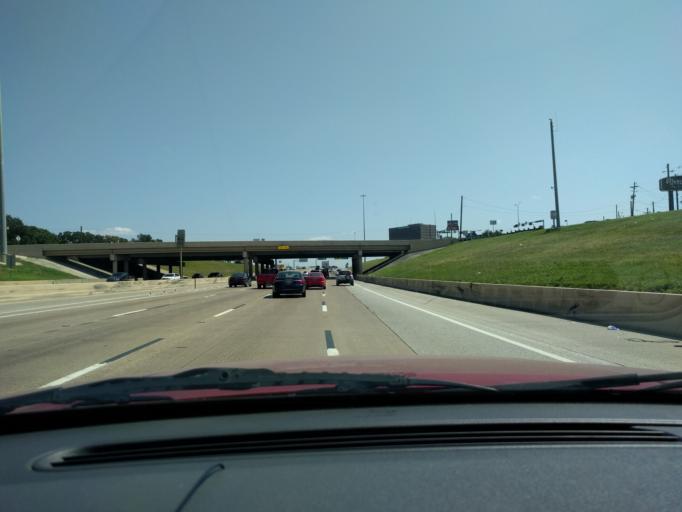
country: US
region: Texas
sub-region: Dallas County
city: Richardson
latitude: 32.9174
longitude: -96.7446
